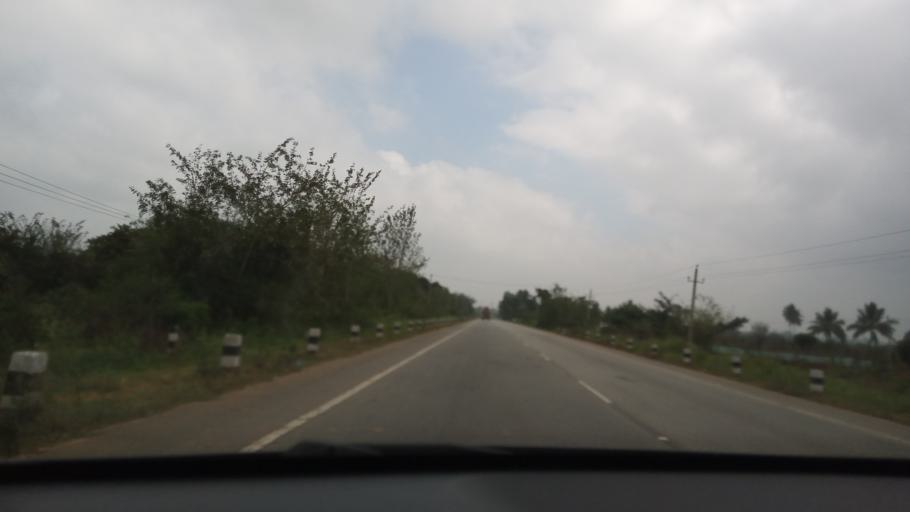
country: IN
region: Karnataka
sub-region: Chikkaballapur
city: Chintamani
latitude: 13.3639
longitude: 78.0473
